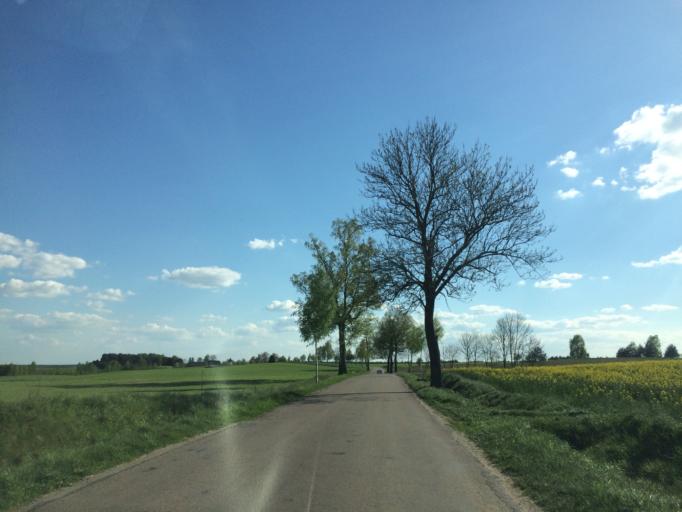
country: PL
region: Warmian-Masurian Voivodeship
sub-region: Powiat dzialdowski
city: Rybno
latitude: 53.4099
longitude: 19.9372
